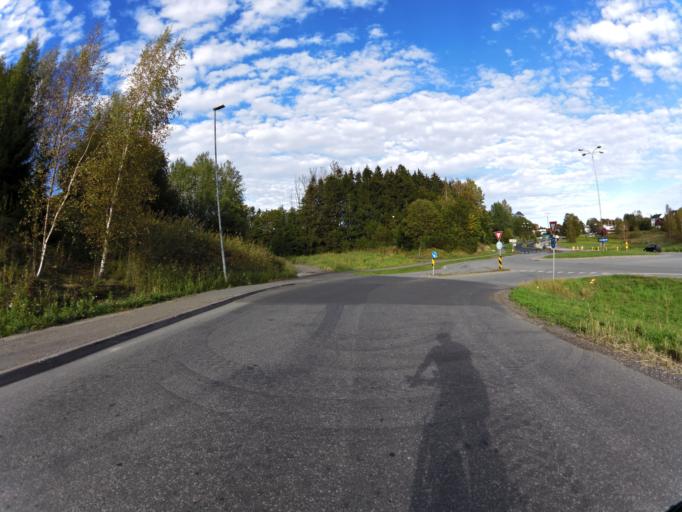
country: NO
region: Ostfold
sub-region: Sarpsborg
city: Sarpsborg
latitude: 59.2829
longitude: 11.0947
